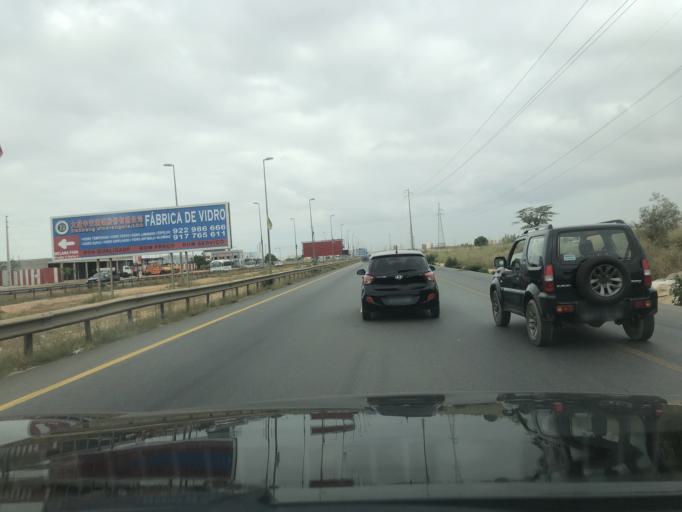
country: AO
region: Luanda
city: Luanda
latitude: -8.9735
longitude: 13.2306
